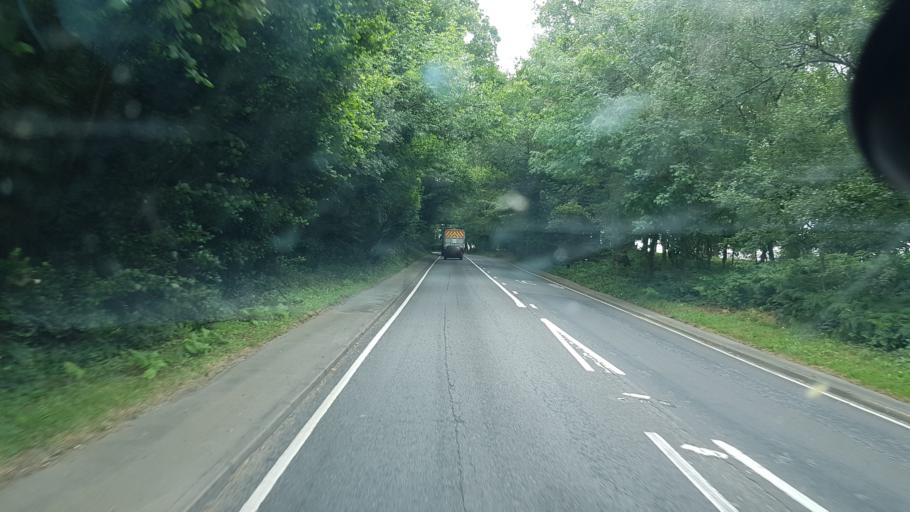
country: GB
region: England
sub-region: Surrey
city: Godstone
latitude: 51.2272
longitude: -0.0471
